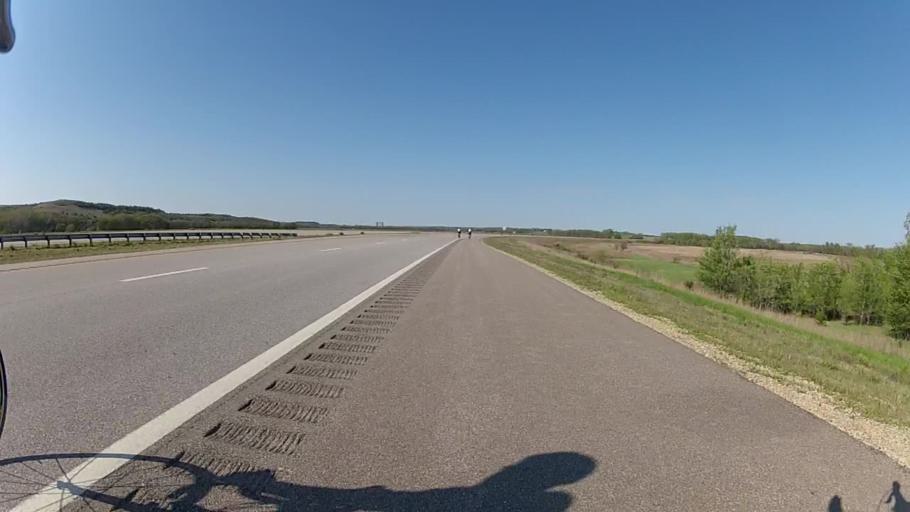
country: US
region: Kansas
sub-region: Riley County
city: Ogden
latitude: 39.0887
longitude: -96.7150
